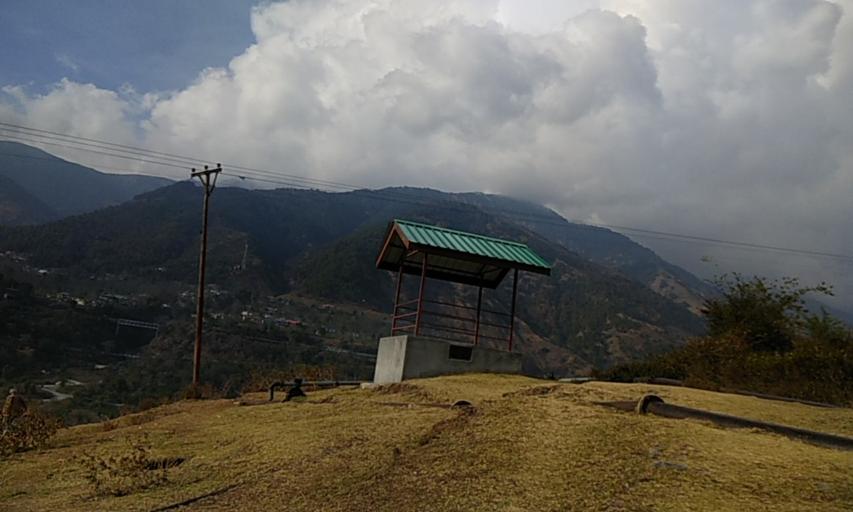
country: IN
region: Himachal Pradesh
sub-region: Kangra
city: Palampur
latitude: 32.1426
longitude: 76.5389
